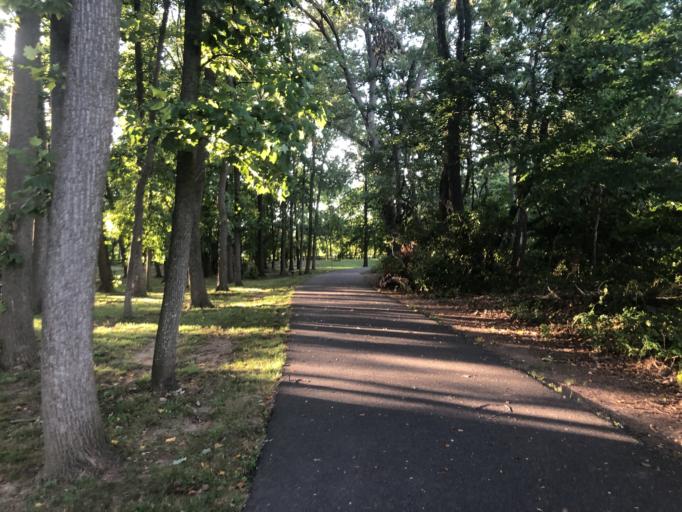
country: US
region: Maryland
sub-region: Harford County
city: Edgewood
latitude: 39.3964
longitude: -76.3485
